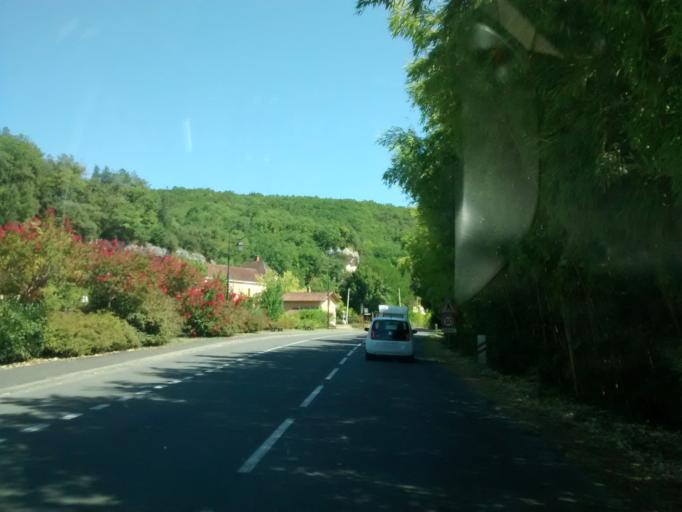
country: FR
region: Aquitaine
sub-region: Departement de la Dordogne
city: Saint-Cyprien
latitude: 44.9406
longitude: 1.0084
